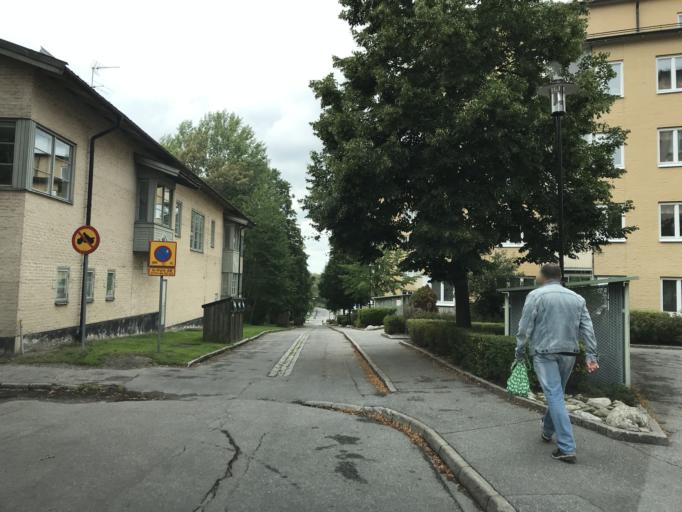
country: SE
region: Stockholm
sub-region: Sundbybergs Kommun
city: Sundbyberg
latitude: 59.3397
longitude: 17.9776
